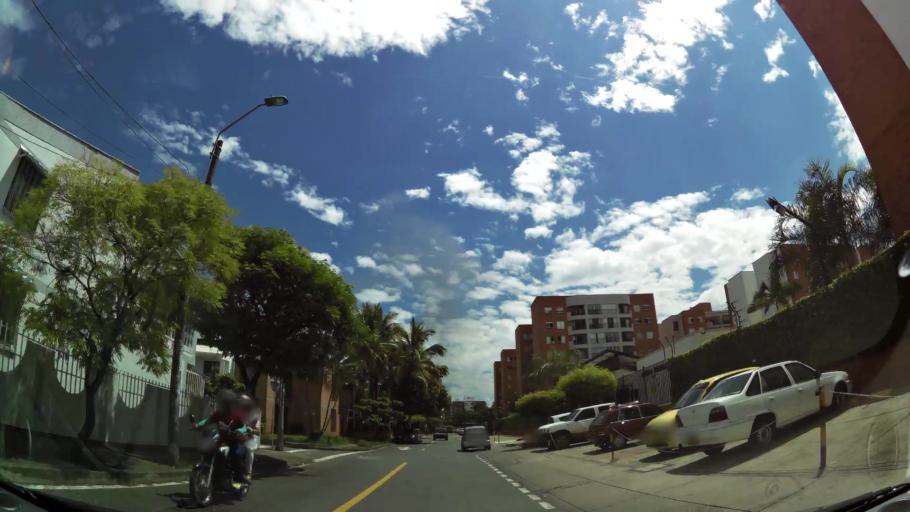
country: CO
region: Valle del Cauca
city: Cali
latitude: 3.3818
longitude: -76.5234
